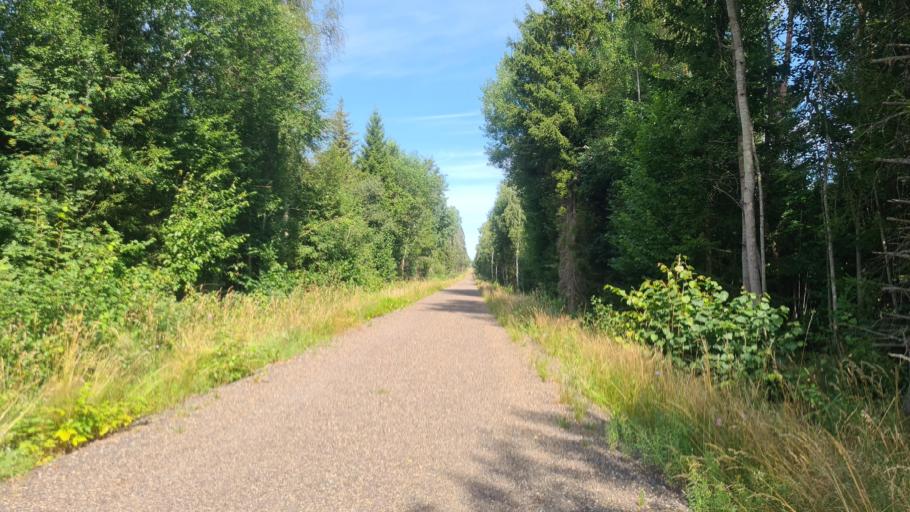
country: SE
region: Kronoberg
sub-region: Ljungby Kommun
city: Lagan
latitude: 56.9729
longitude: 13.9497
